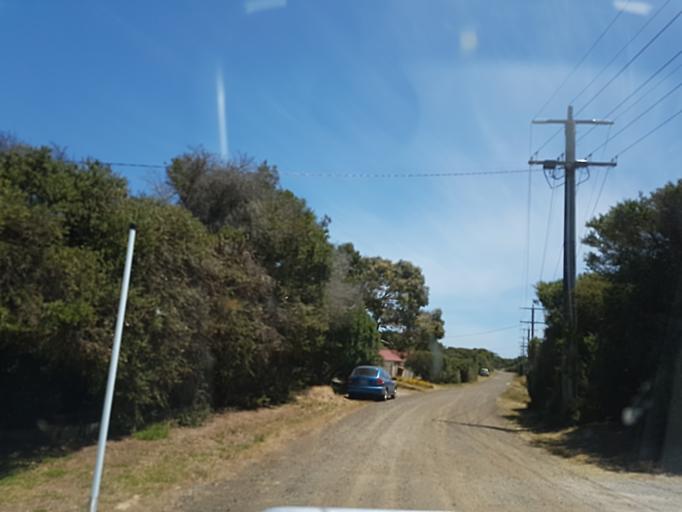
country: AU
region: Victoria
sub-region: Bass Coast
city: North Wonthaggi
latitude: -38.7001
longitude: 145.8237
